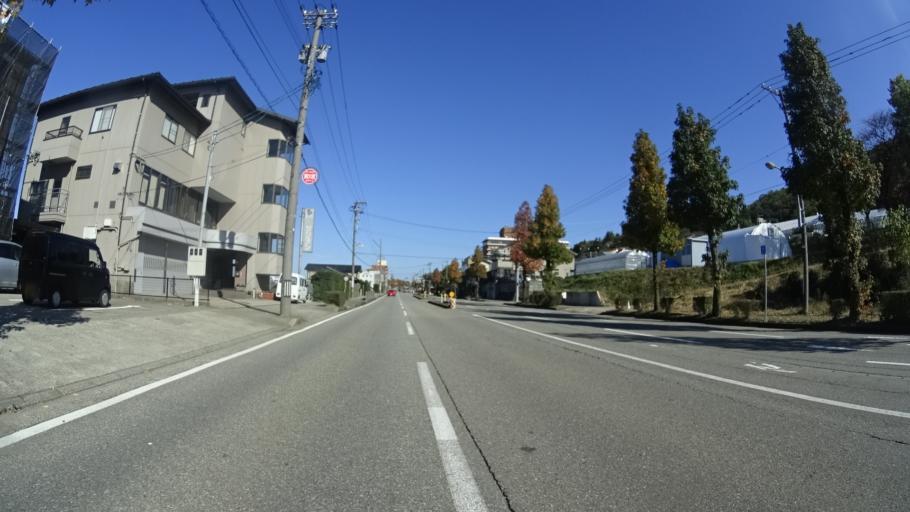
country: JP
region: Ishikawa
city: Nonoichi
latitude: 36.5116
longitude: 136.6292
